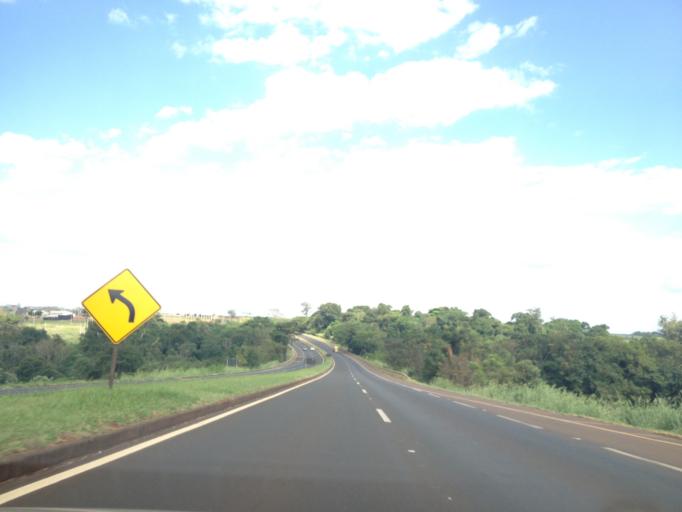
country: BR
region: Parana
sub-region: Marialva
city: Marialva
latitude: -23.4871
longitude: -51.8193
